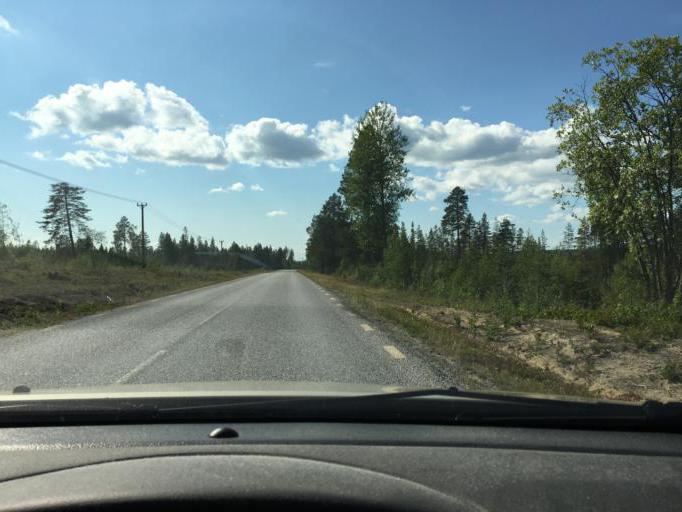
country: SE
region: Norrbotten
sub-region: Kalix Kommun
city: Toere
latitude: 66.0636
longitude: 22.6320
